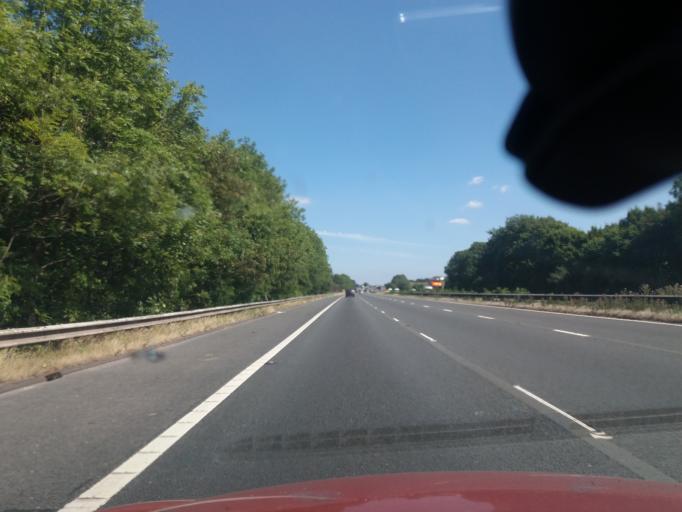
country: GB
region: England
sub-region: Borough of Bolton
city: Westhoughton
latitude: 53.5611
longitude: -2.5071
